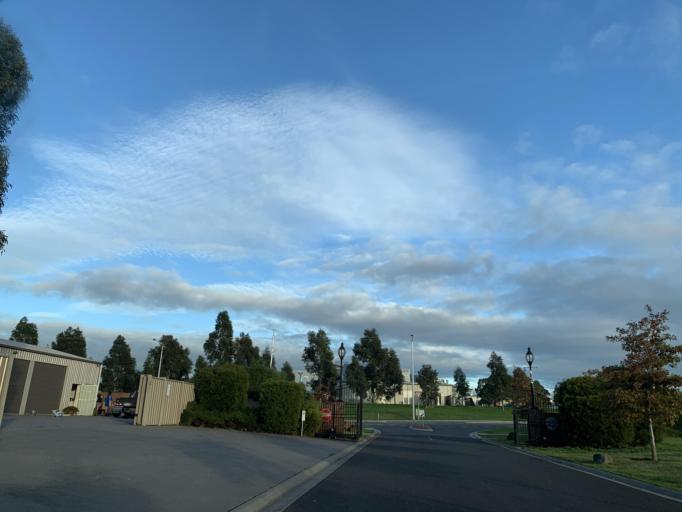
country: AU
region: Victoria
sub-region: Casey
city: Cranbourne East
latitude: -38.1138
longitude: 145.3000
